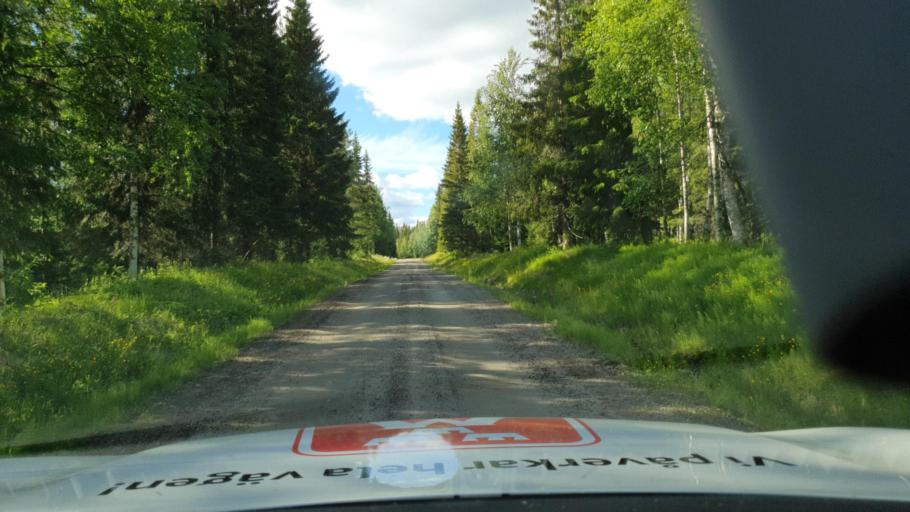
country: SE
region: Vaesterbotten
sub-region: Lycksele Kommun
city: Lycksele
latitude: 64.4088
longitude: 18.2902
